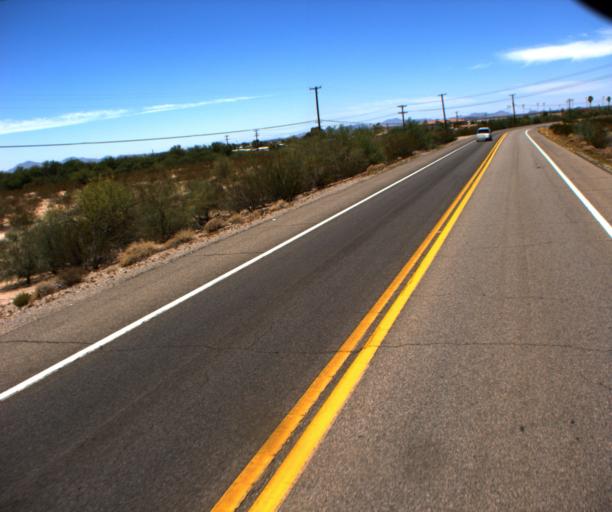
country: US
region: Arizona
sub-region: Pinal County
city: Florence
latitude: 33.0162
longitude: -111.3844
